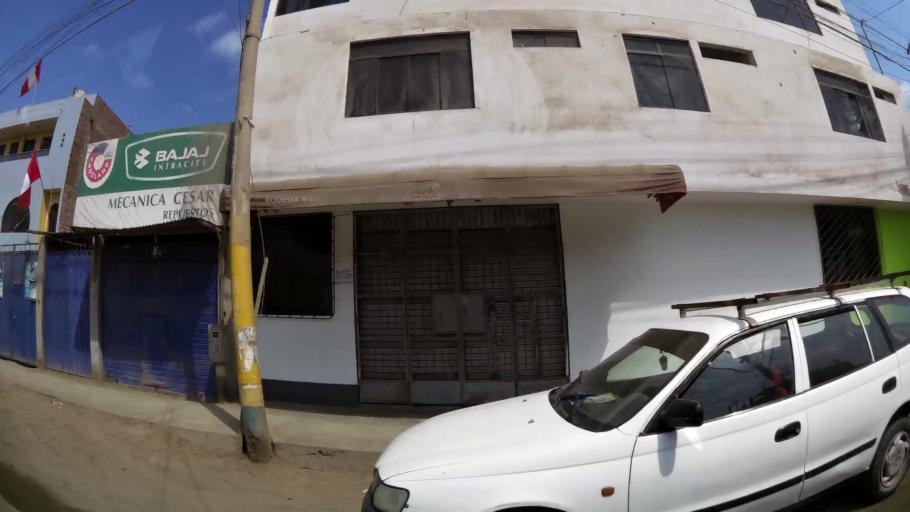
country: PE
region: Lima
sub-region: Provincia de Canete
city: Mala
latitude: -12.6536
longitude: -76.6333
